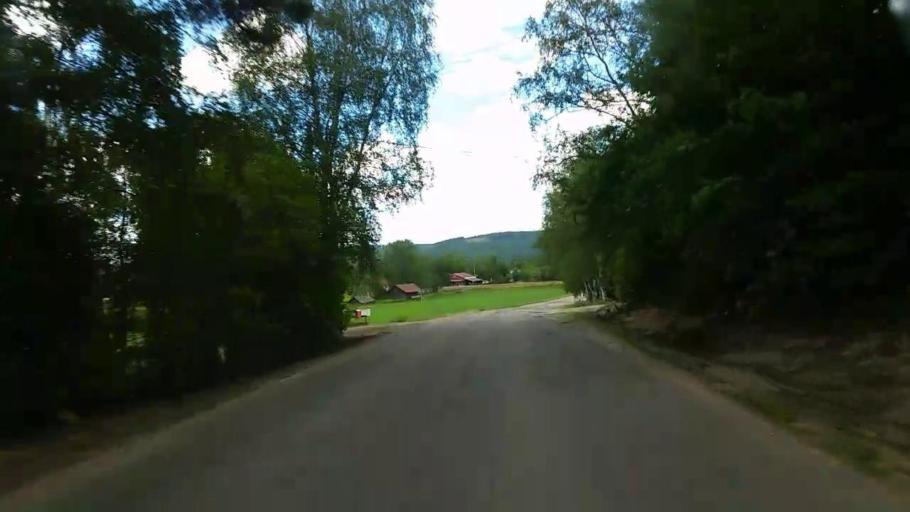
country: SE
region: Gaevleborg
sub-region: Ljusdals Kommun
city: Jaervsoe
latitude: 61.6715
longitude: 16.1401
